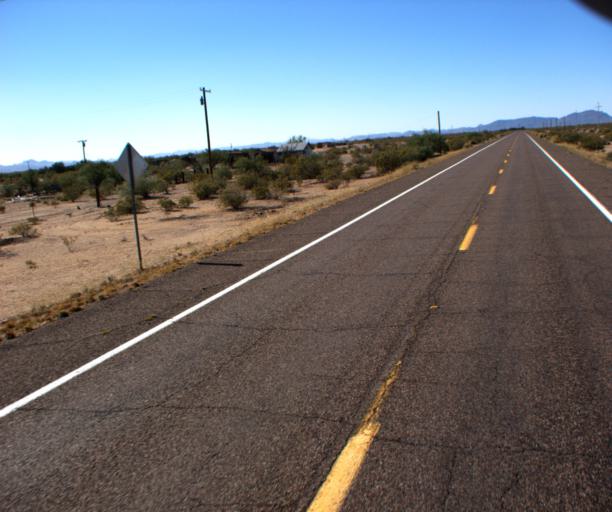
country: US
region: Arizona
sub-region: Maricopa County
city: Gila Bend
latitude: 32.9243
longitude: -112.7345
